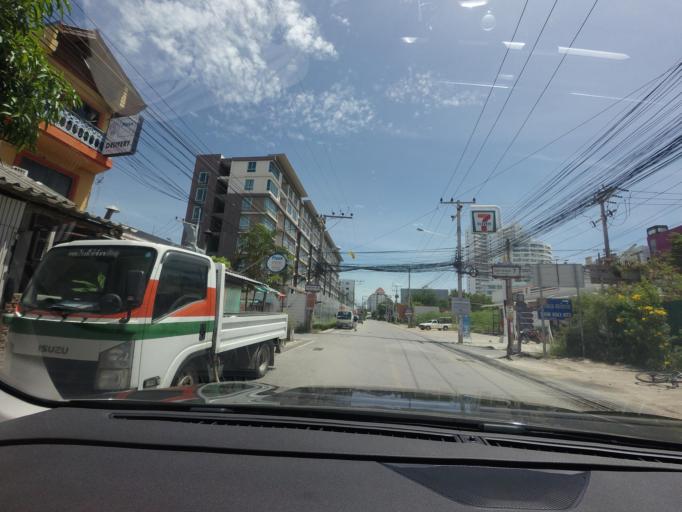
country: TH
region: Prachuap Khiri Khan
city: Hua Hin
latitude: 12.5136
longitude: 99.9760
